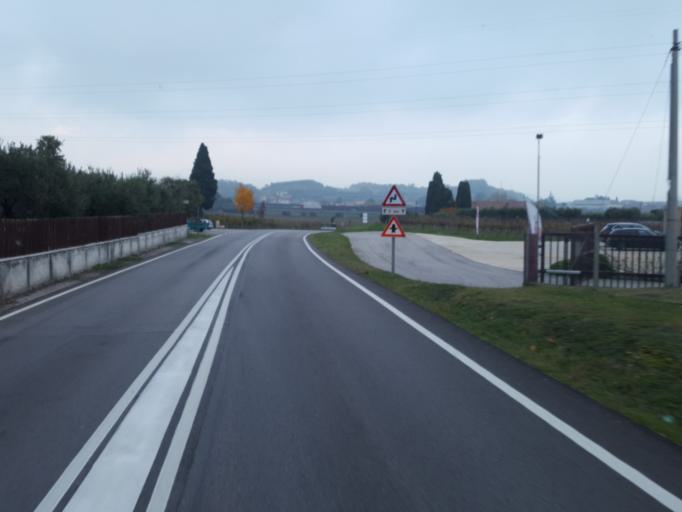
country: IT
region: Veneto
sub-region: Provincia di Verona
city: Pastrengo
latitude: 45.5086
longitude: 10.7786
